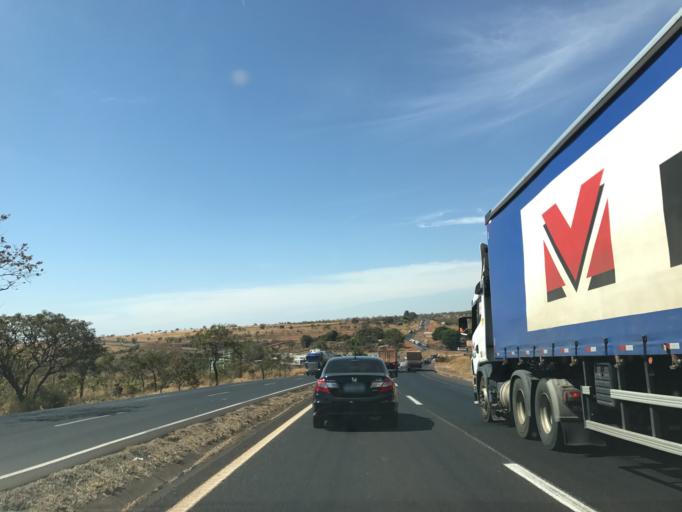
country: BR
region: Minas Gerais
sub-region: Monte Alegre De Minas
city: Monte Alegre de Minas
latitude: -18.8740
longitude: -49.0597
